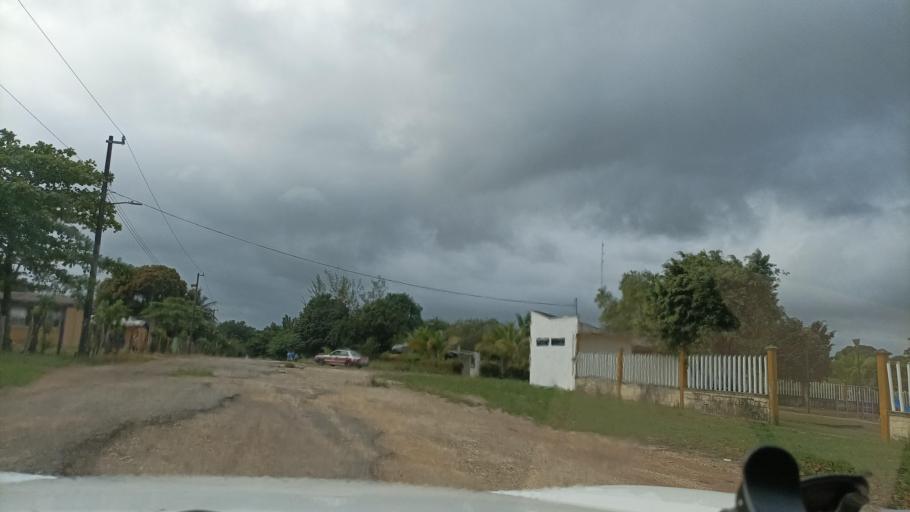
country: MX
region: Veracruz
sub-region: Moloacan
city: Cuichapa
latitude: 17.9227
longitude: -94.3683
